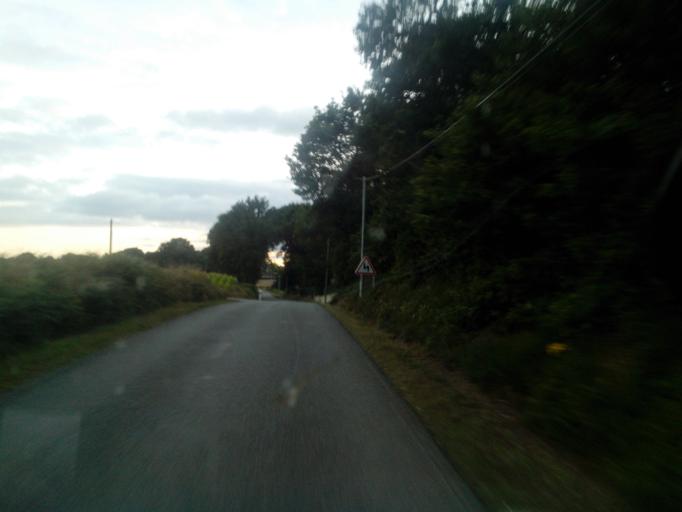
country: FR
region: Brittany
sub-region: Departement du Morbihan
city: Plumelec
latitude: 47.8963
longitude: -2.6316
